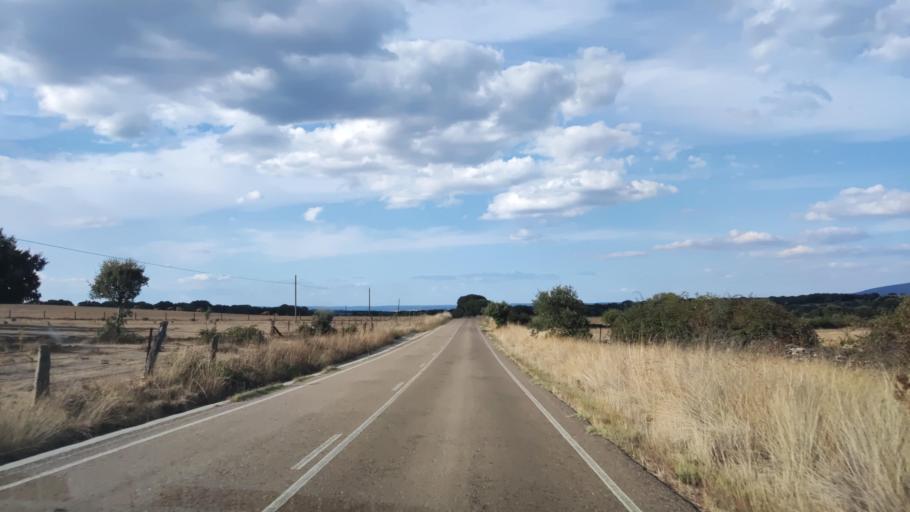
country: ES
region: Castille and Leon
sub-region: Provincia de Salamanca
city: Martiago
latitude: 40.4653
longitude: -6.4896
